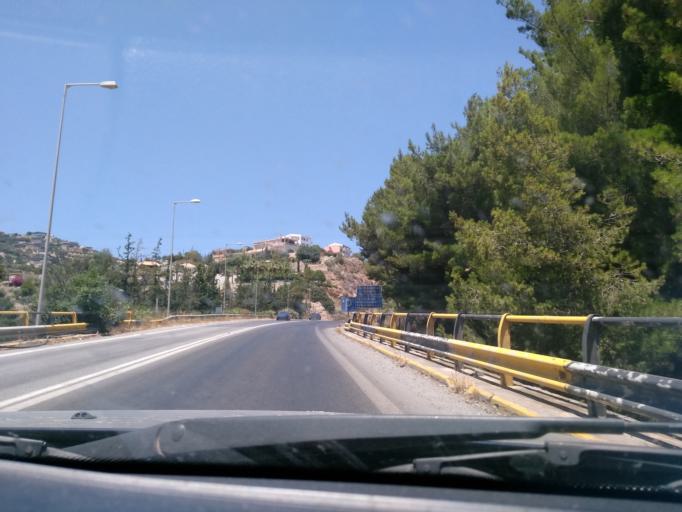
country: GR
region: Crete
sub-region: Nomos Irakleiou
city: Gazi
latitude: 35.3536
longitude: 25.0411
